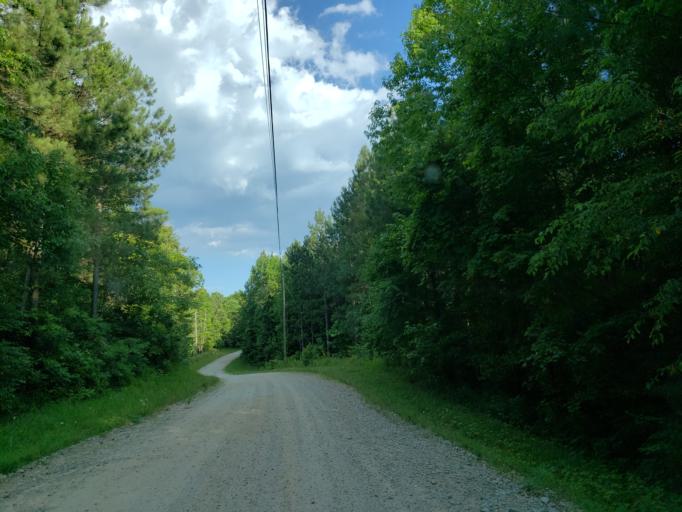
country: US
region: Georgia
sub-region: Haralson County
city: Buchanan
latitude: 33.9002
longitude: -85.3084
